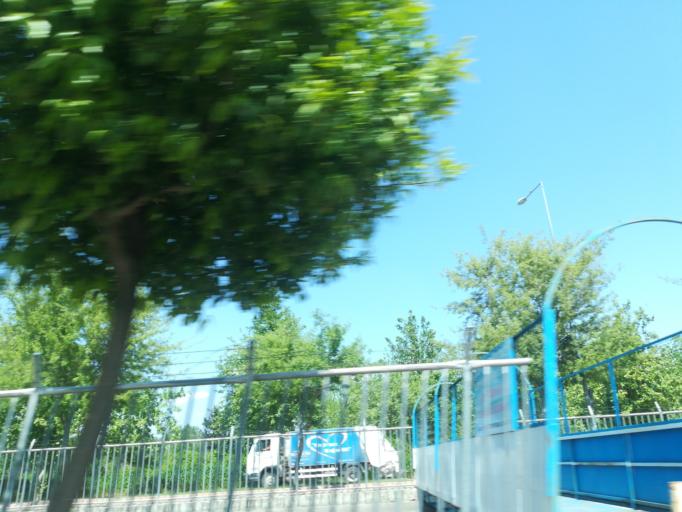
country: TR
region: Adana
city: Adana
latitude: 37.0207
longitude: 35.3719
